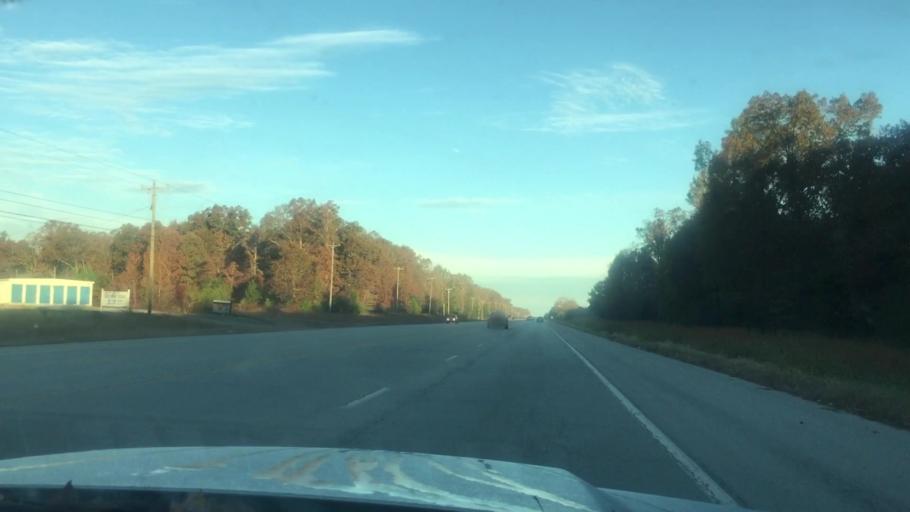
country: US
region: Tennessee
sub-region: Franklin County
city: Estill Springs
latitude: 35.3016
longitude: -86.1552
